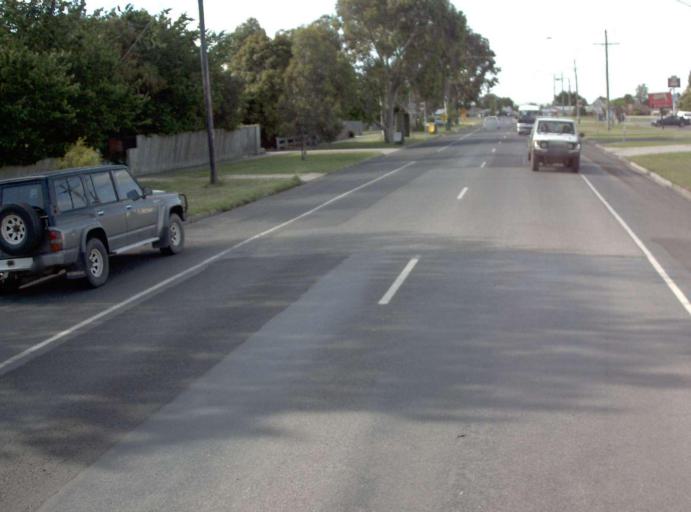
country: AU
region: Victoria
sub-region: Bass Coast
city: North Wonthaggi
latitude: -38.5964
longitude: 145.5922
